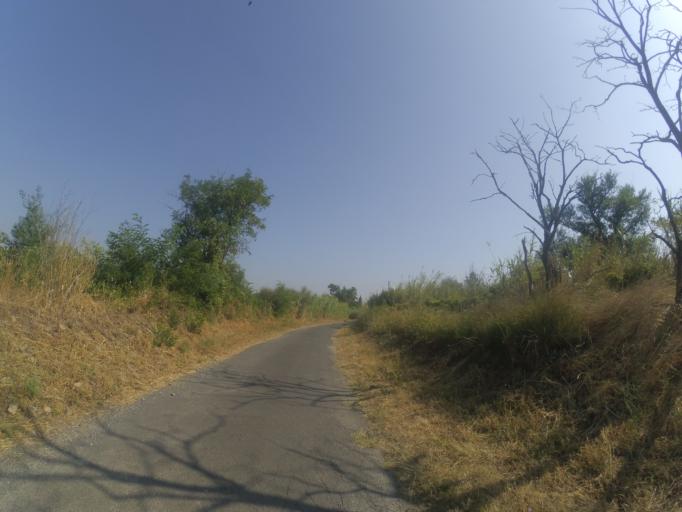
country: FR
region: Languedoc-Roussillon
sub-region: Departement des Pyrenees-Orientales
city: Ille-sur-Tet
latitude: 42.6596
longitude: 2.6252
